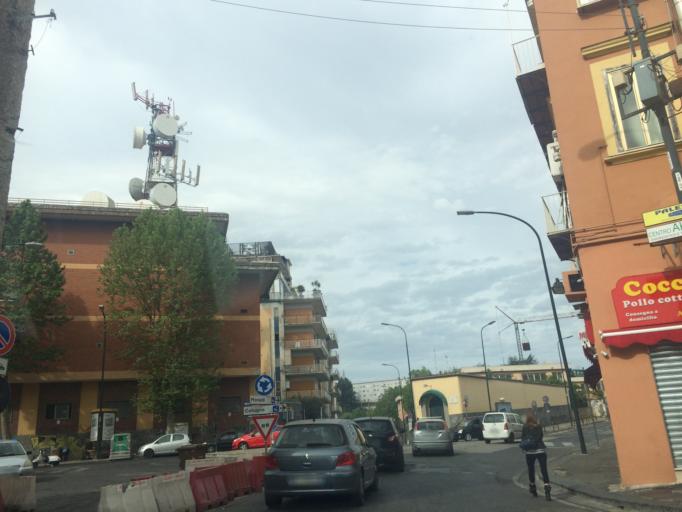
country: IT
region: Campania
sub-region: Provincia di Napoli
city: Napoli
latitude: 40.8641
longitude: 14.2198
